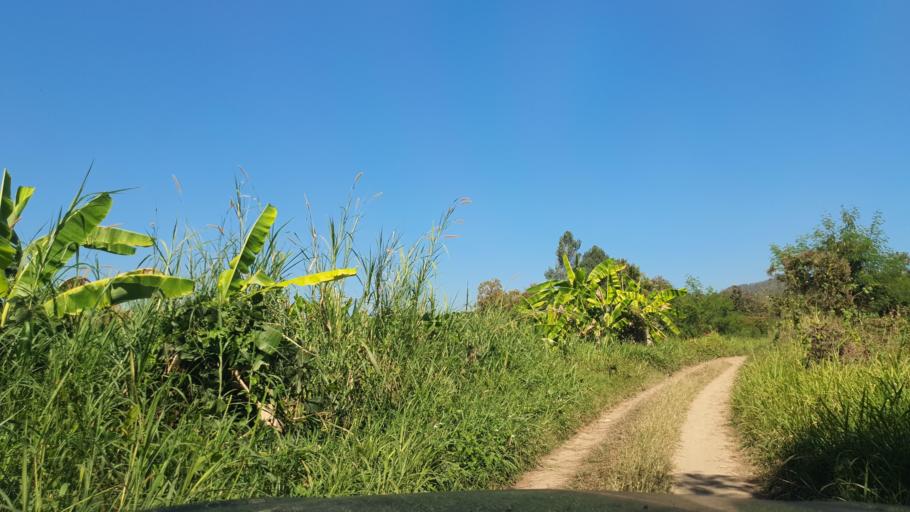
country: TH
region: Chiang Mai
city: Mae Wang
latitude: 18.6719
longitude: 98.8260
